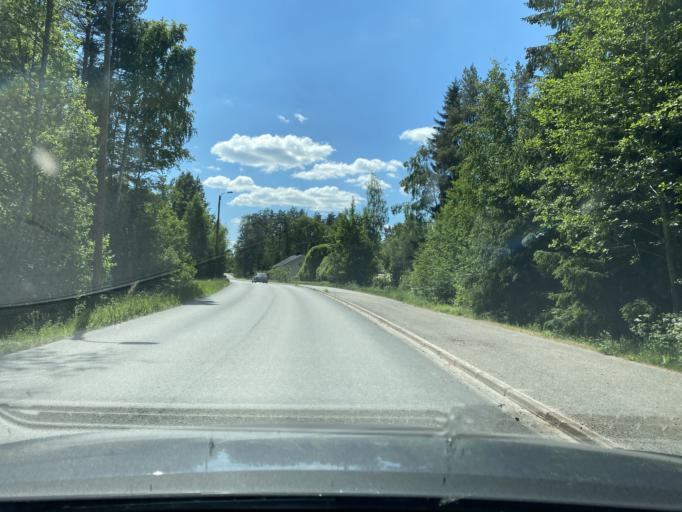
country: FI
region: Satakunta
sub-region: Rauma
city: Eura
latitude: 61.1288
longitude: 22.1641
